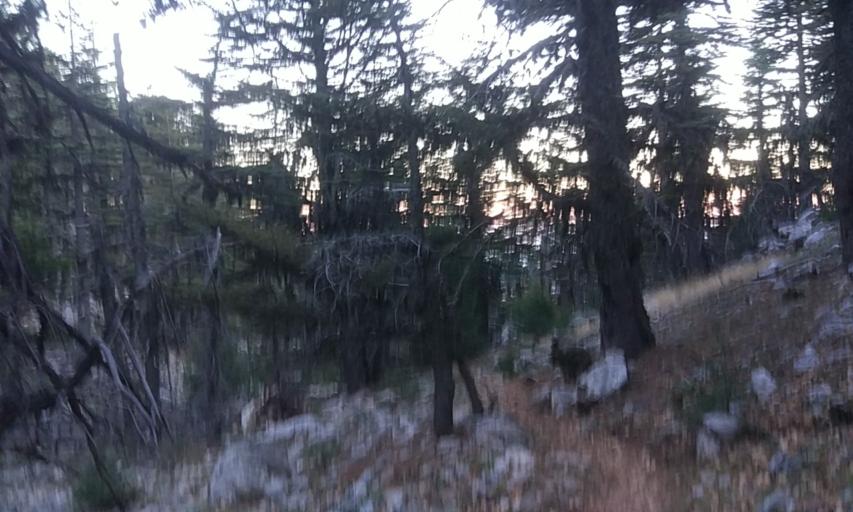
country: TR
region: Antalya
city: Altinyaka
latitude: 36.5372
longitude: 30.4171
